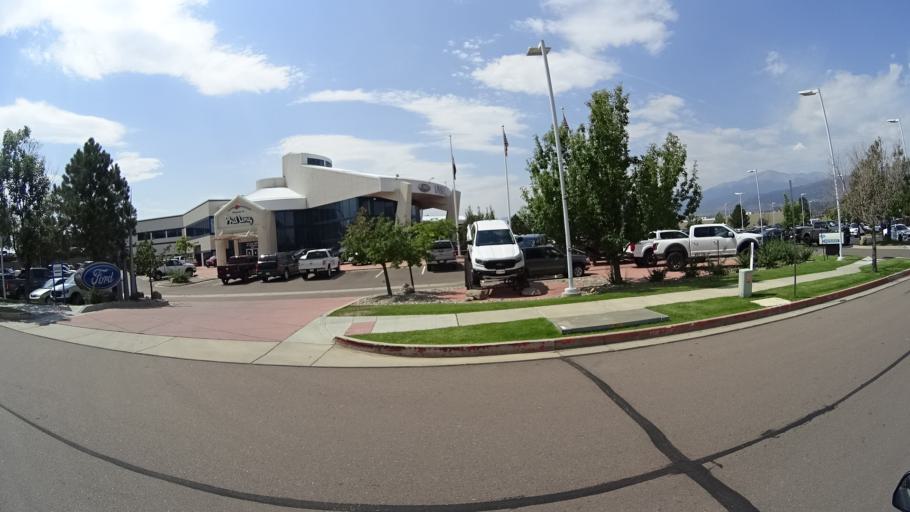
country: US
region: Colorado
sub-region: El Paso County
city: Air Force Academy
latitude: 38.9532
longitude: -104.7958
